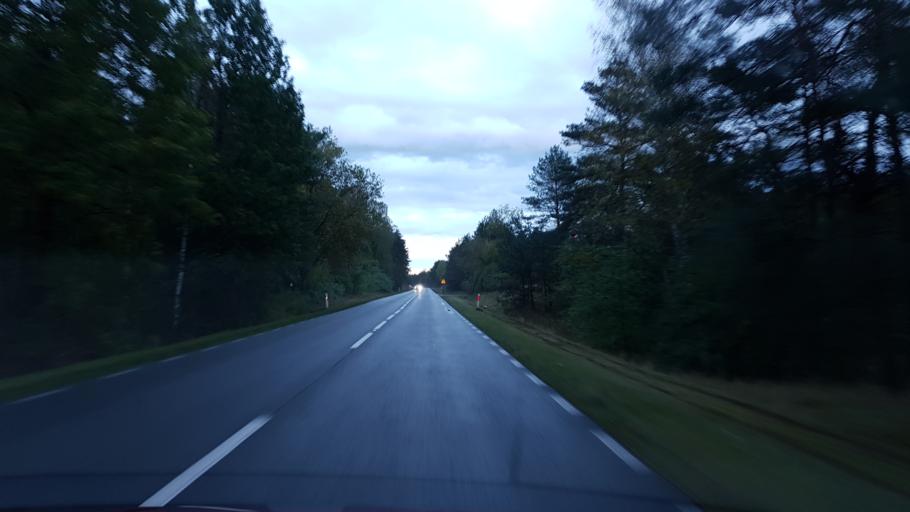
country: PL
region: Greater Poland Voivodeship
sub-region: Powiat pilski
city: Smilowo
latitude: 53.2126
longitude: 16.8582
